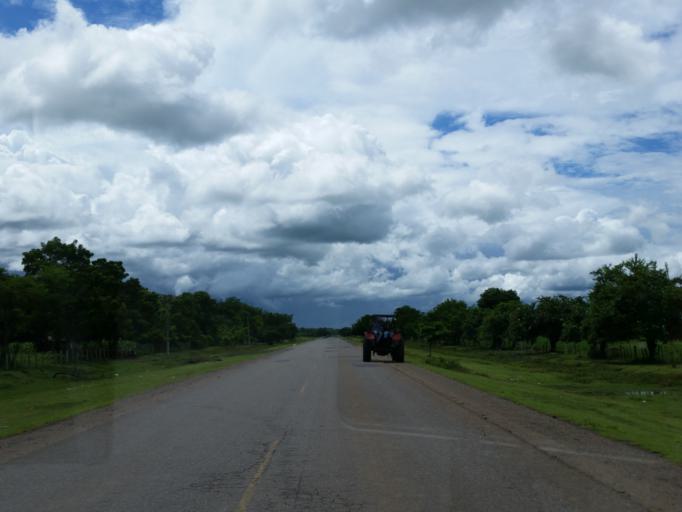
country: NI
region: Chinandega
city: Chichigalpa
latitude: 12.7898
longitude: -86.9222
